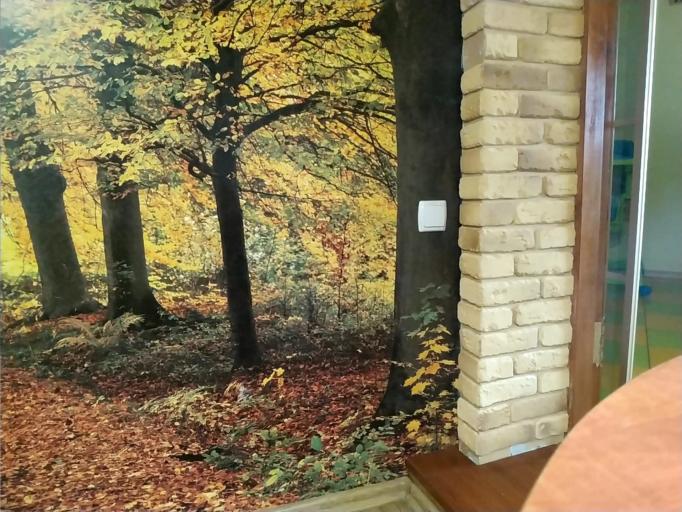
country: RU
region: Smolensk
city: Dorogobuzh
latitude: 54.8982
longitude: 33.3175
